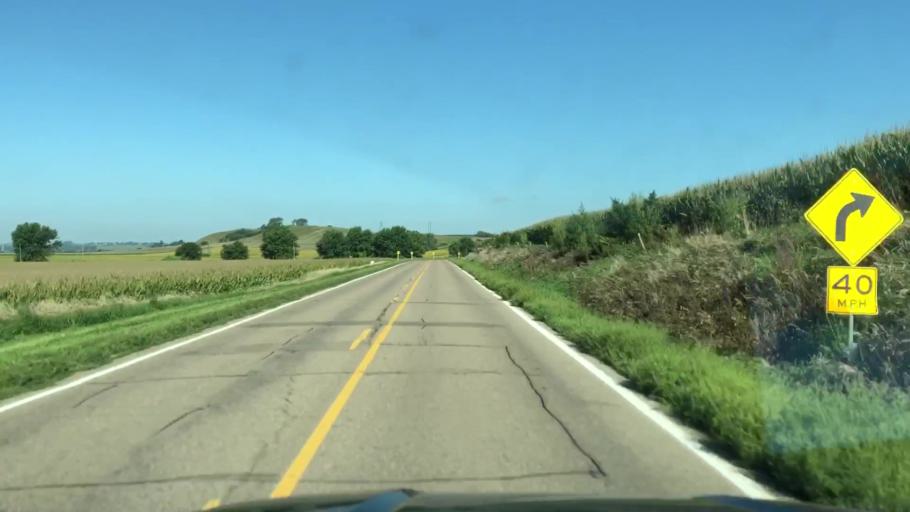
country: US
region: Iowa
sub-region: Woodbury County
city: Sergeant Bluff
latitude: 42.4076
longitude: -96.2536
